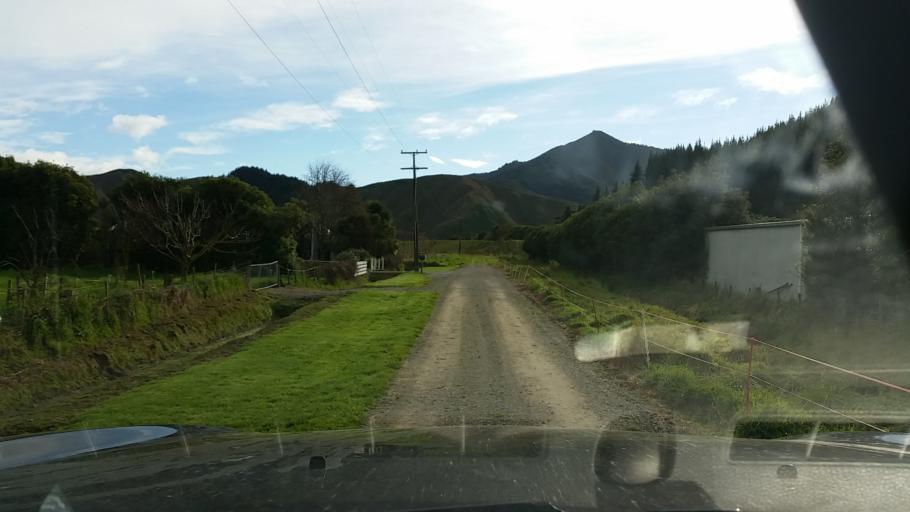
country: NZ
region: Marlborough
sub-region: Marlborough District
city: Blenheim
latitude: -41.4249
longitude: 173.9579
